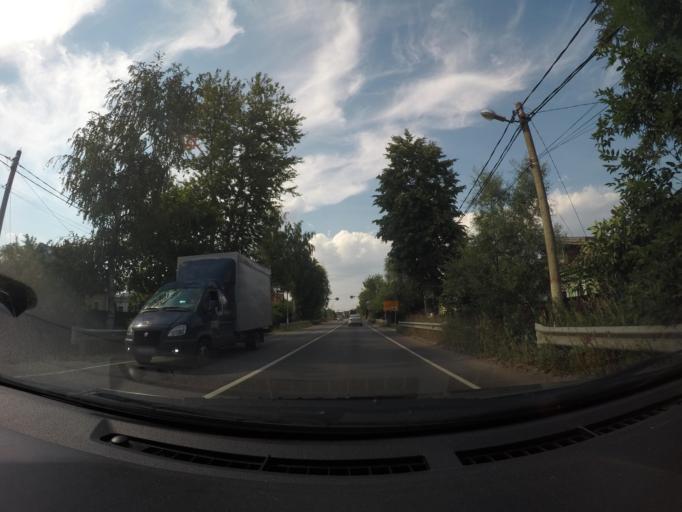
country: RU
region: Moskovskaya
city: Gzhel'
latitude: 55.6229
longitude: 38.3756
